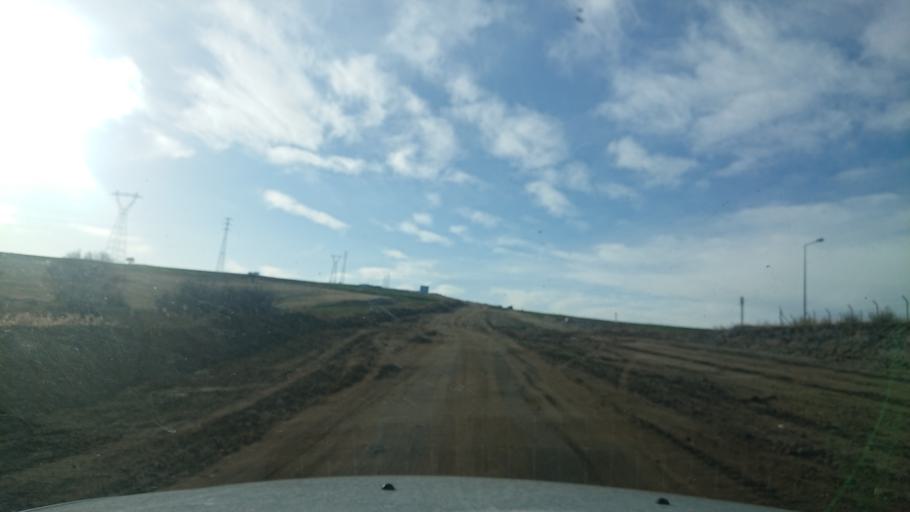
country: TR
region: Aksaray
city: Agacoren
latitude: 38.8537
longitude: 33.9428
